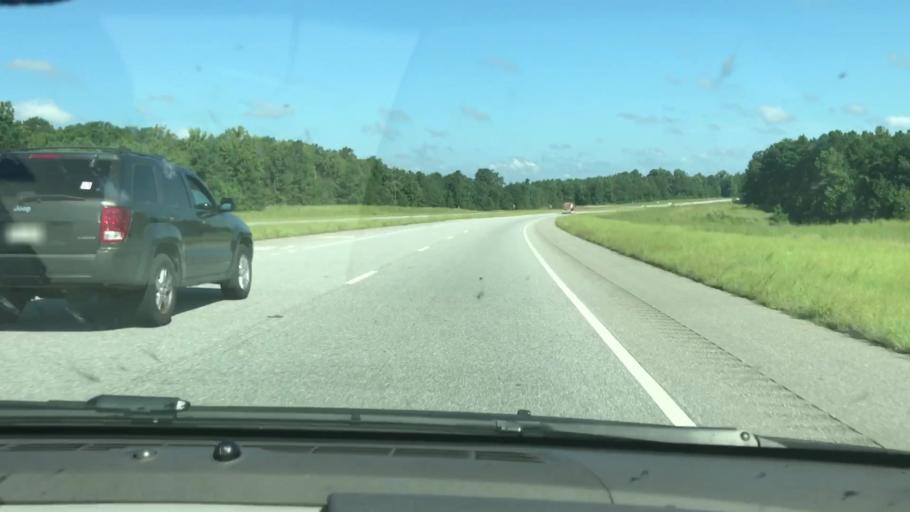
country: US
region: Alabama
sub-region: Barbour County
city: Eufaula
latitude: 32.1523
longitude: -85.1761
